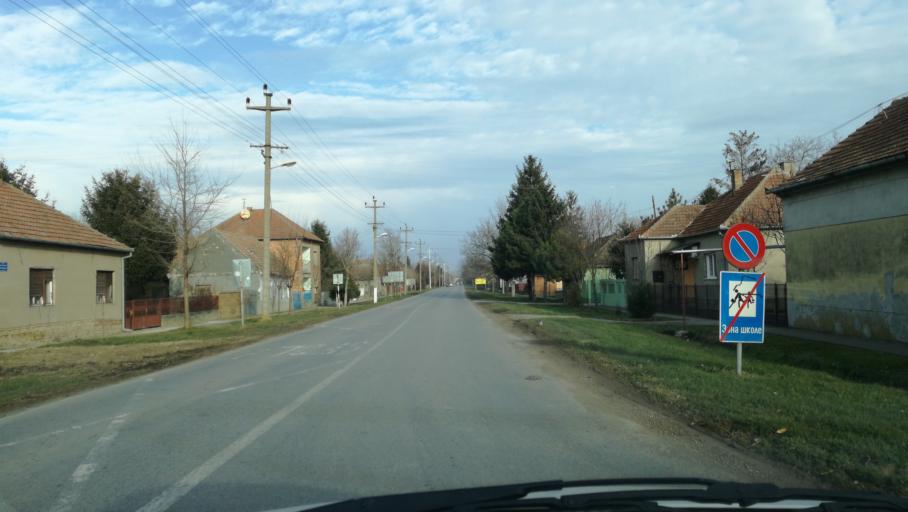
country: RS
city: Rusko Selo
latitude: 45.7592
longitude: 20.5786
